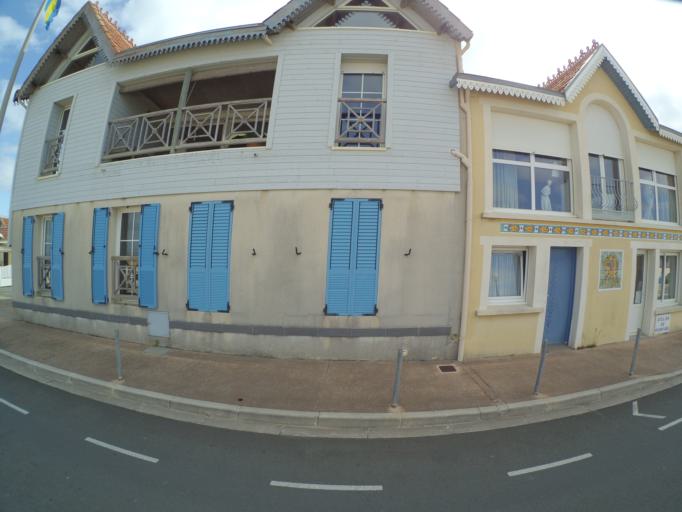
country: FR
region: Poitou-Charentes
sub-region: Departement de la Charente-Maritime
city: Chatelaillon-Plage
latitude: 46.0819
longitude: -1.0961
